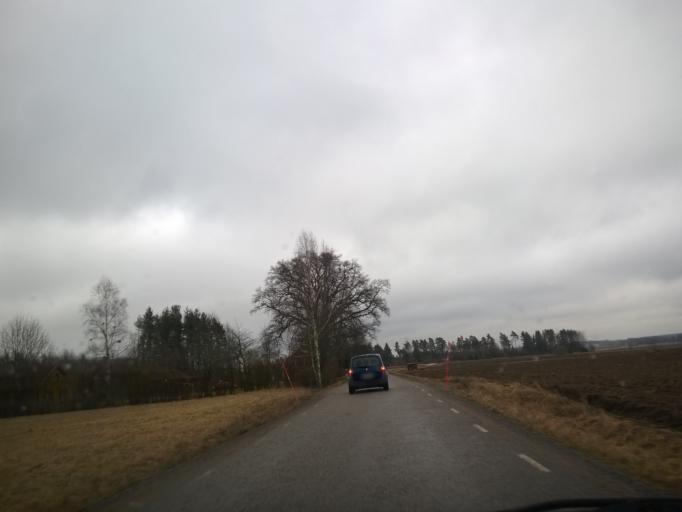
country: SE
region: Uppsala
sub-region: Osthammars Kommun
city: Bjorklinge
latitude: 60.1628
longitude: 17.5264
